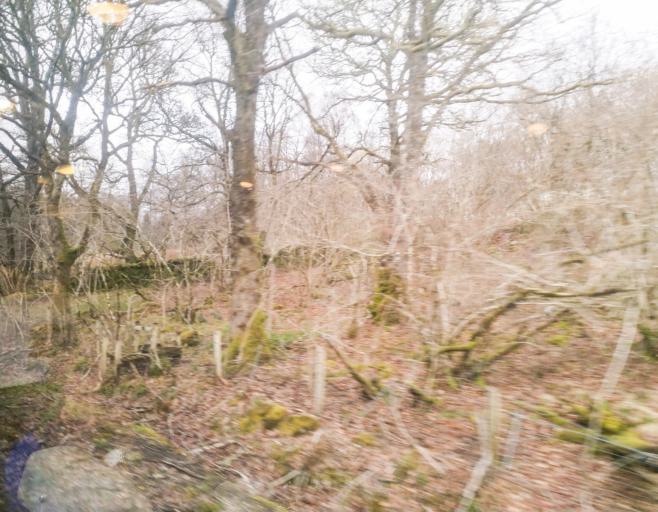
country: GB
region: Scotland
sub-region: Highland
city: Spean Bridge
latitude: 56.8924
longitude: -4.8840
